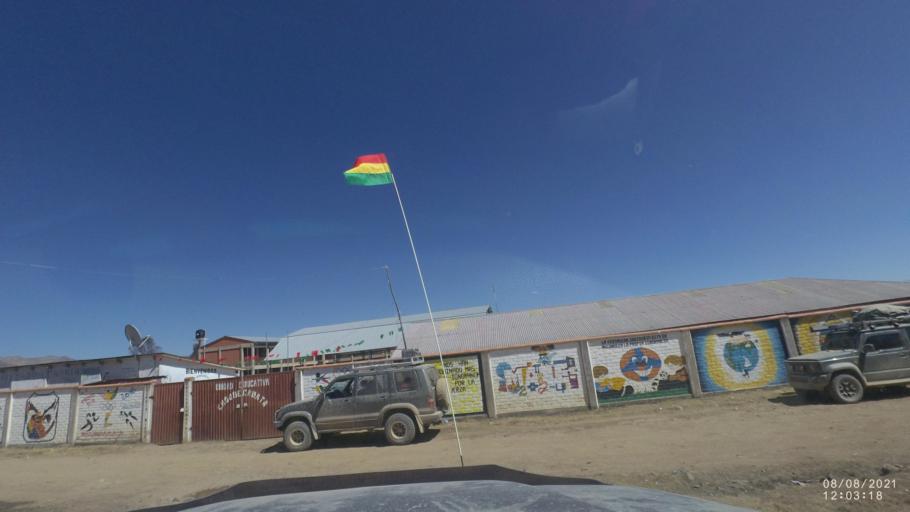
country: BO
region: Cochabamba
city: Colchani
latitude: -16.8383
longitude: -66.6301
